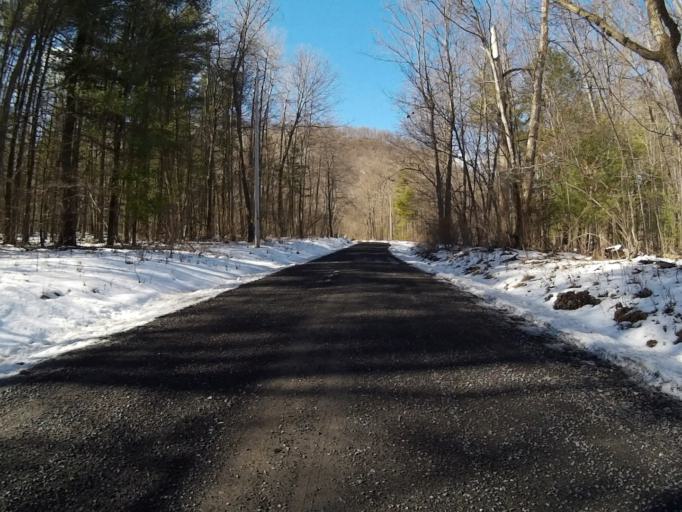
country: US
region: Pennsylvania
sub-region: Centre County
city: Stormstown
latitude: 40.8554
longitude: -78.0531
